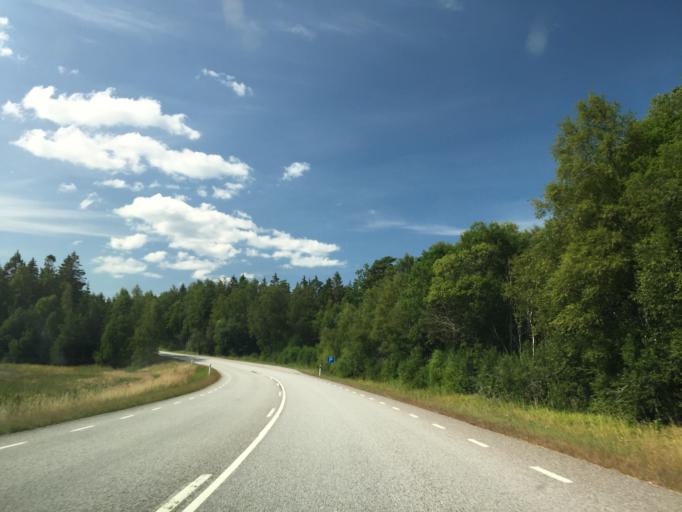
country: SE
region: Vaestra Goetaland
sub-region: Tanums Kommun
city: Tanumshede
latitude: 58.8216
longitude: 11.2582
